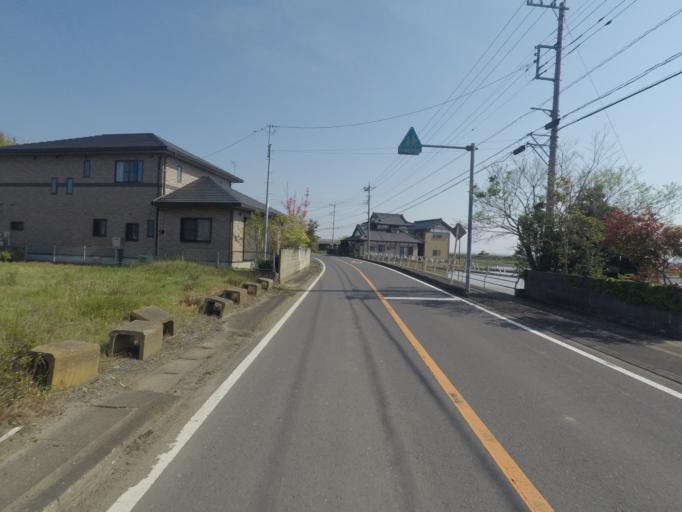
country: JP
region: Ibaraki
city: Itako
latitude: 36.0486
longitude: 140.4489
